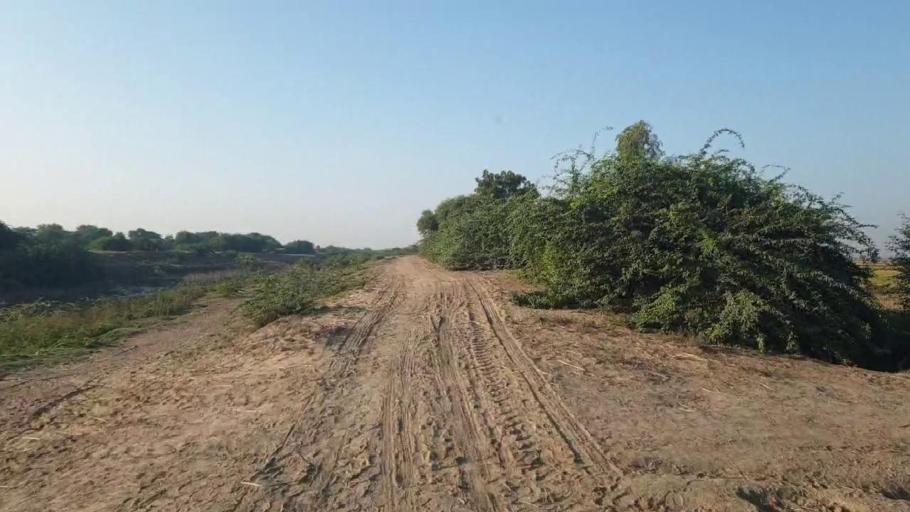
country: PK
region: Sindh
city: Badin
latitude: 24.6174
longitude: 68.7878
